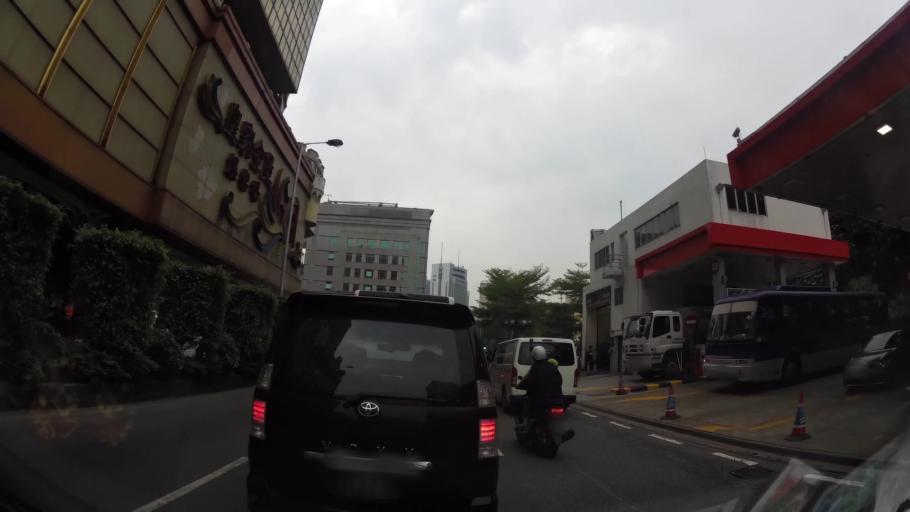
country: MO
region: Macau
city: Macau
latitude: 22.1970
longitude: 113.5534
